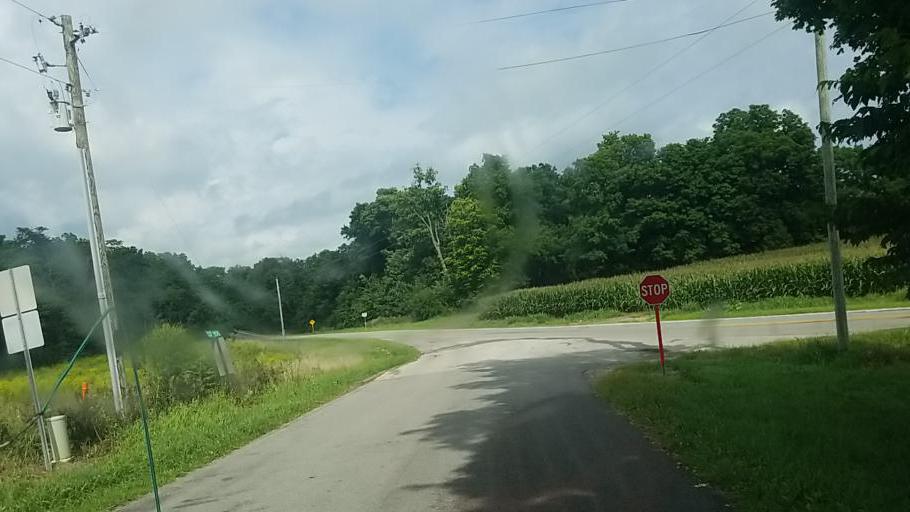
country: US
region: Ohio
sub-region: Champaign County
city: North Lewisburg
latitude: 40.2686
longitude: -83.6061
